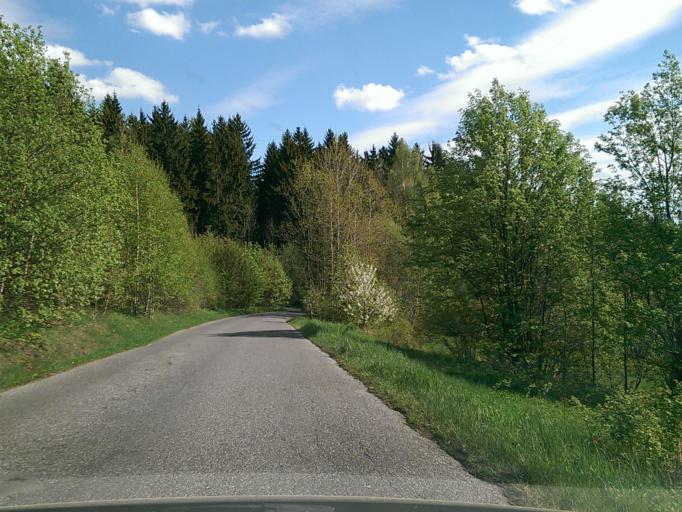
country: CZ
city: Pencin
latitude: 50.6649
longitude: 15.2360
